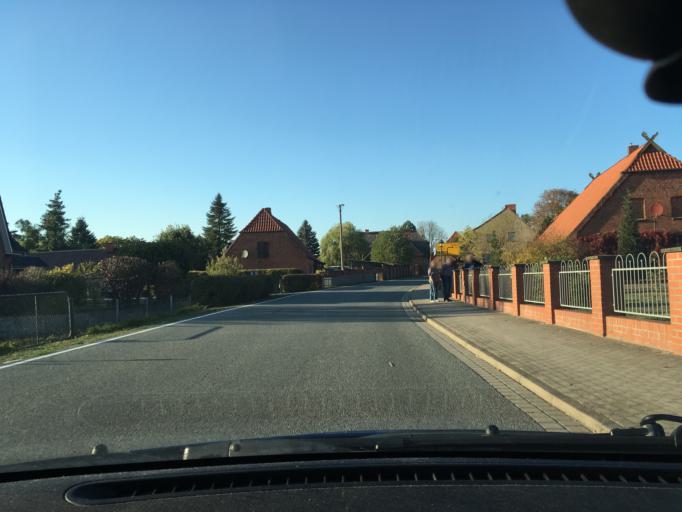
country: DE
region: Lower Saxony
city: Neu Darchau
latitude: 53.2793
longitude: 10.9333
